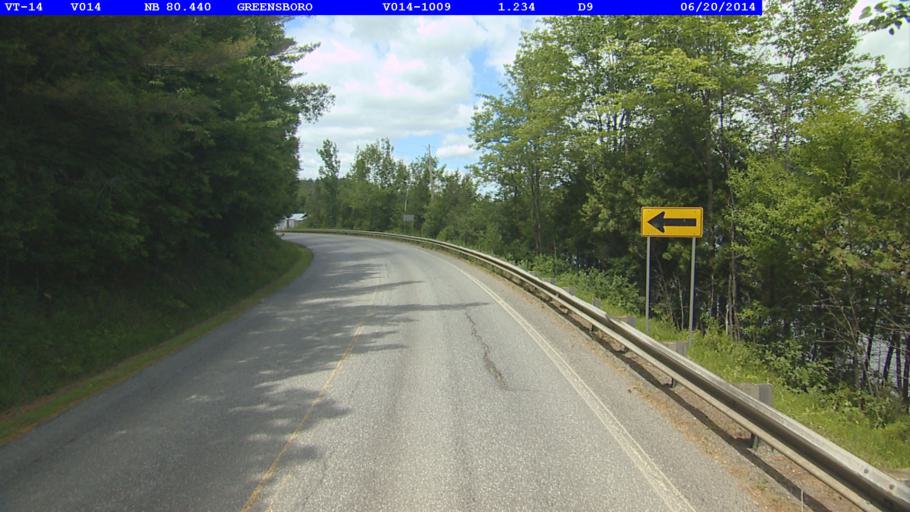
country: US
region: Vermont
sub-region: Caledonia County
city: Hardwick
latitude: 44.5968
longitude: -72.3578
